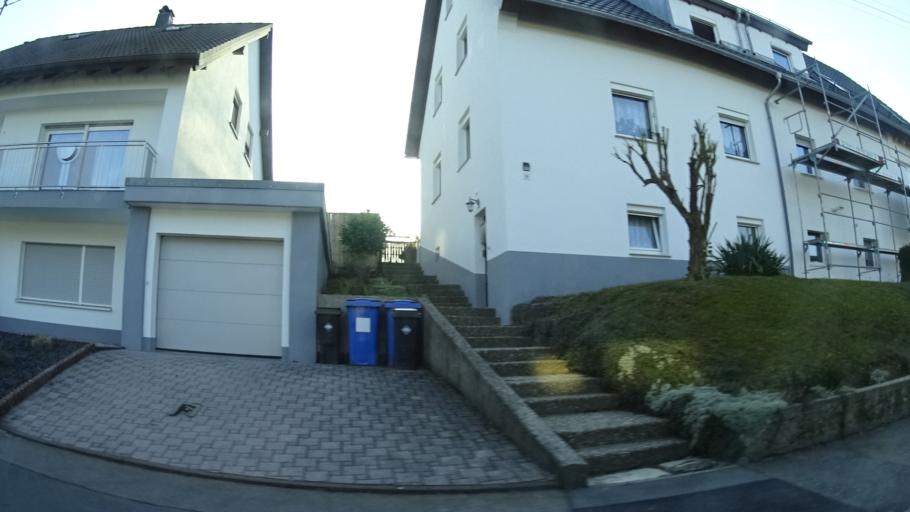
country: DE
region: Baden-Wuerttemberg
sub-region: Karlsruhe Region
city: Mosbach
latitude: 49.3498
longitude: 9.1696
